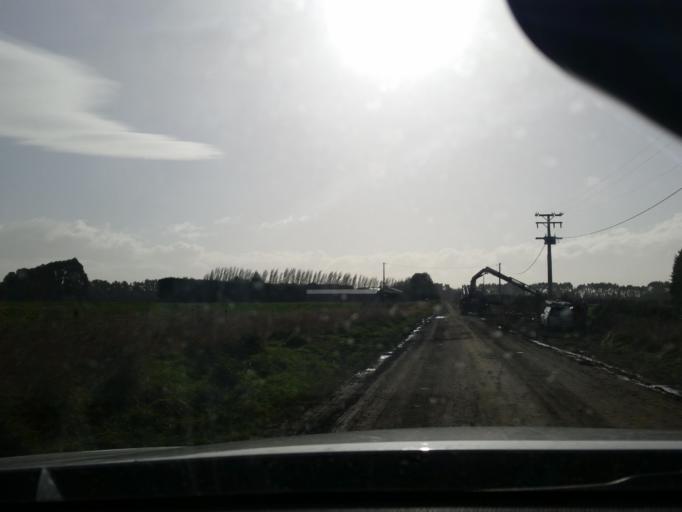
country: NZ
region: Southland
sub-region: Invercargill City
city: Invercargill
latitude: -46.2810
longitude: 168.2942
